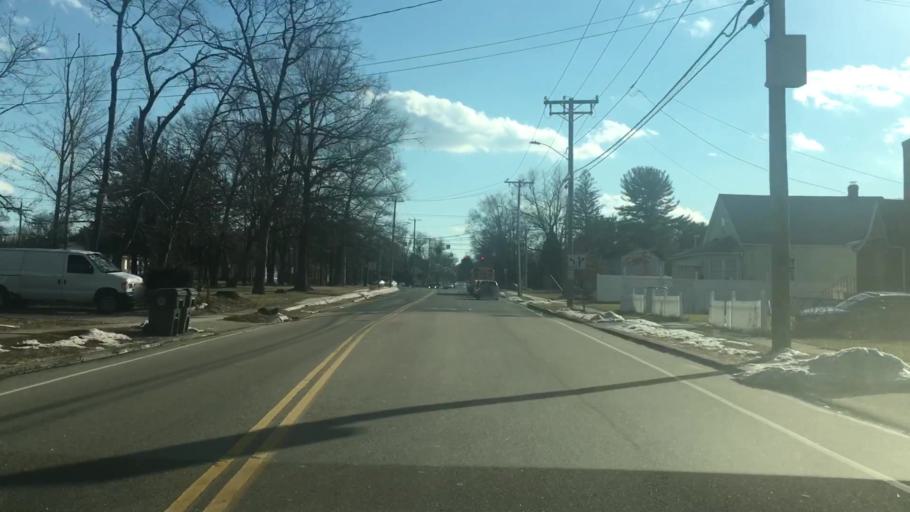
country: US
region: Connecticut
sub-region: Hartford County
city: East Hartford
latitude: 41.7671
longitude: -72.6004
